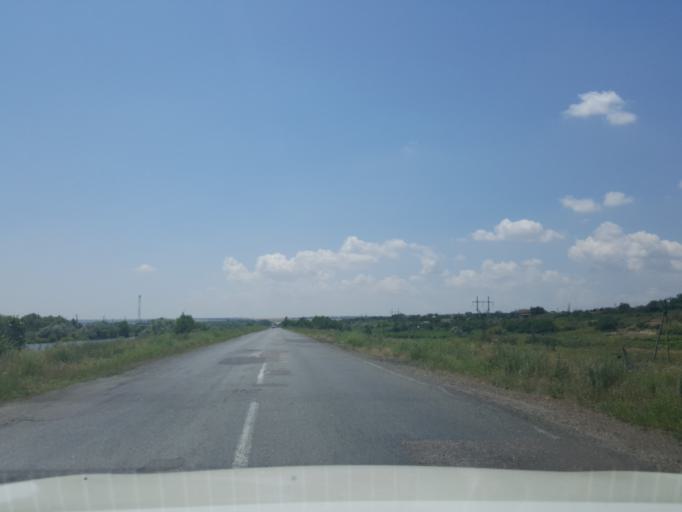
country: UA
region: Odessa
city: Bilyayivka
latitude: 46.4085
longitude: 30.1076
